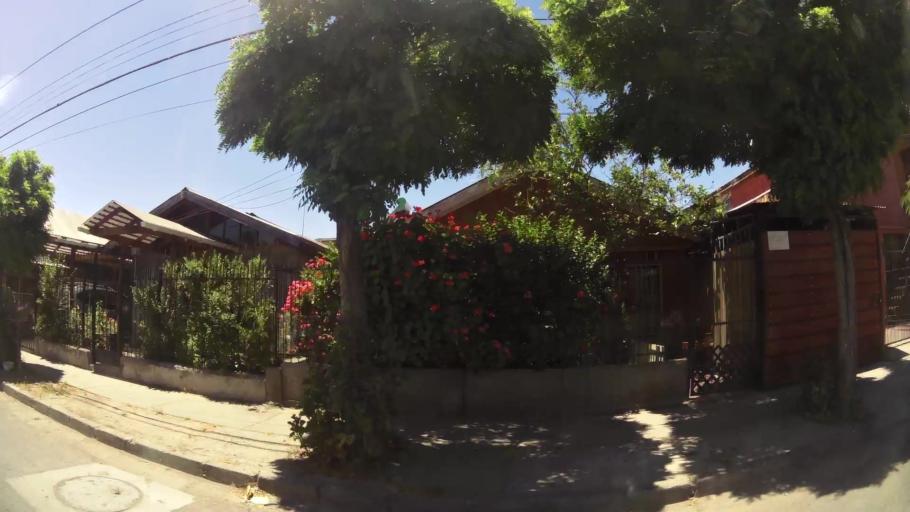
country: CL
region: Santiago Metropolitan
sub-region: Provincia de Santiago
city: La Pintana
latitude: -33.5576
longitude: -70.6421
